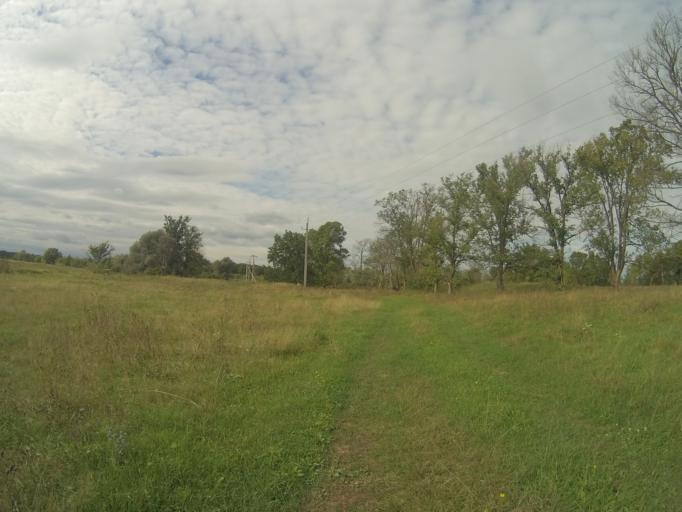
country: RU
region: Vladimir
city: Raduzhnyy
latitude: 56.0377
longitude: 40.2922
